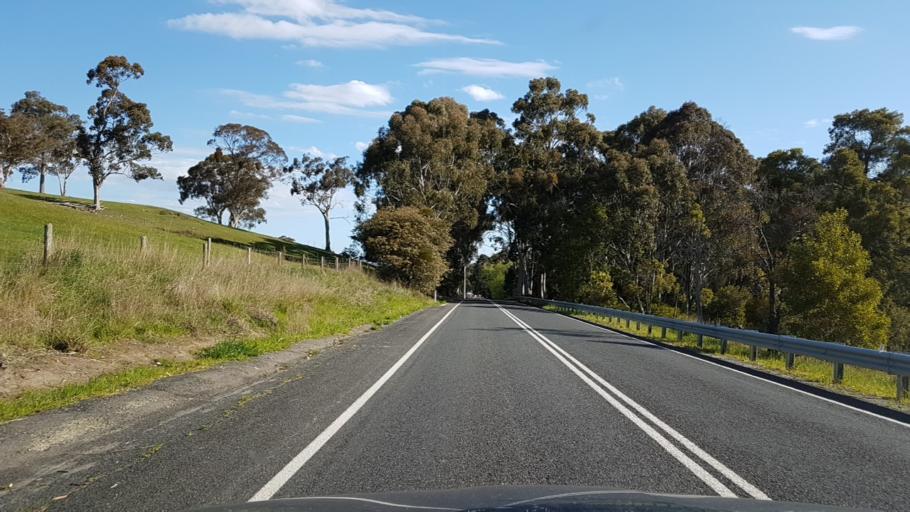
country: AU
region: South Australia
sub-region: Adelaide Hills
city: Lobethal
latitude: -34.8863
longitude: 138.8812
